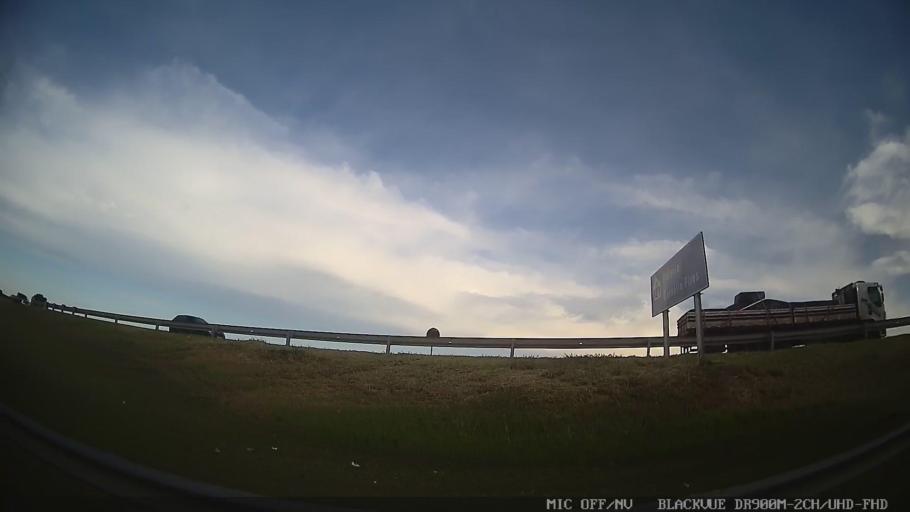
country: BR
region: Sao Paulo
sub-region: Tiete
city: Tiete
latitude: -23.0613
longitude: -47.7249
